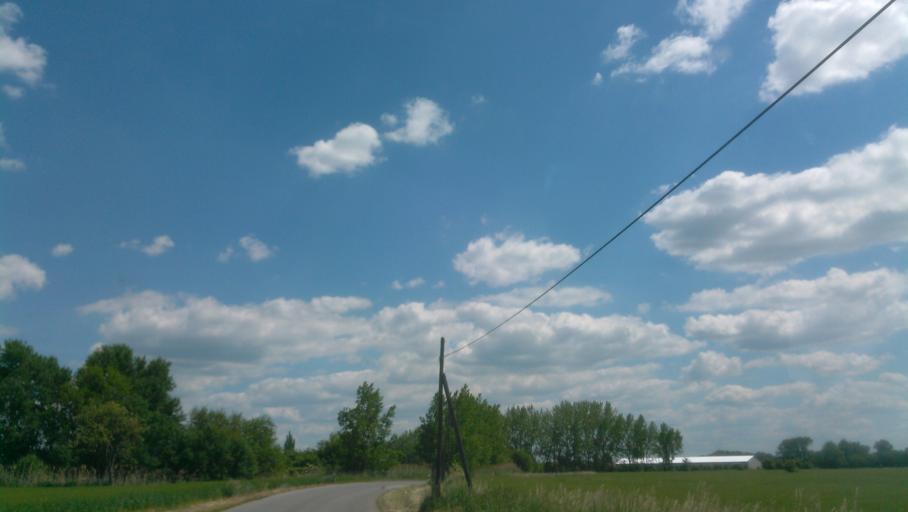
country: SK
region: Nitriansky
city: Kolarovo
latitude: 47.8772
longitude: 17.9139
